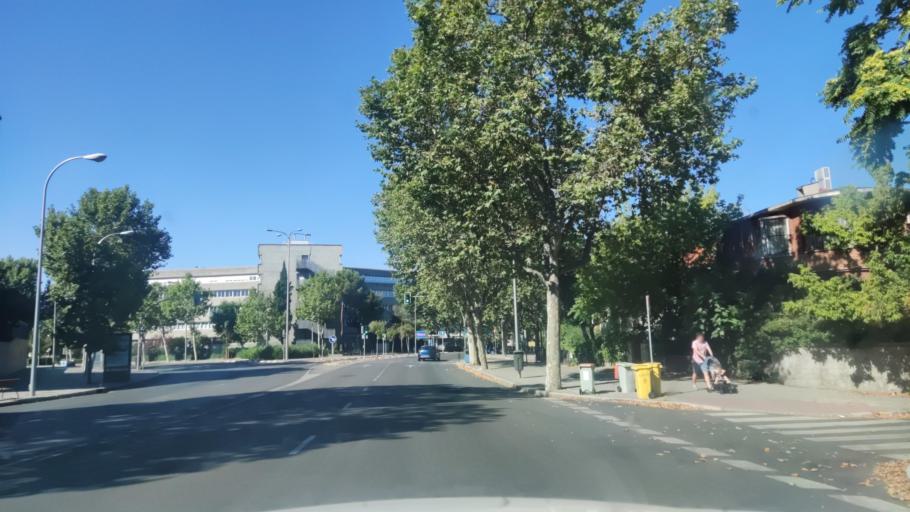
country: ES
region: Madrid
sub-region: Provincia de Madrid
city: Chamartin
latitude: 40.4466
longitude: -3.6819
